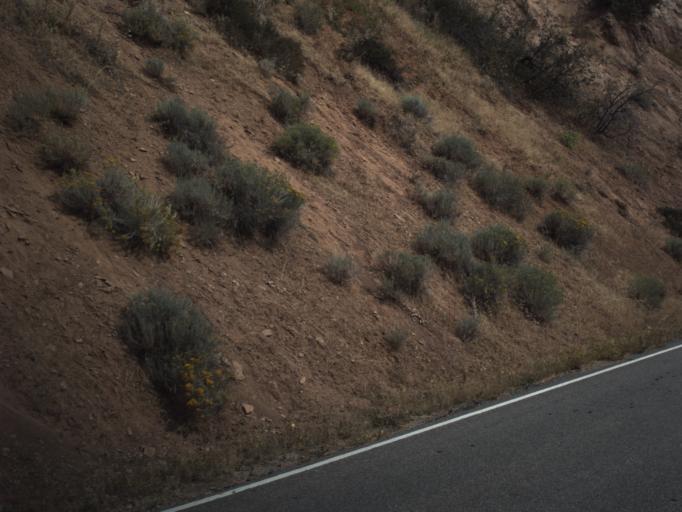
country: US
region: Utah
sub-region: Summit County
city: Summit Park
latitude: 40.8197
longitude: -111.6677
